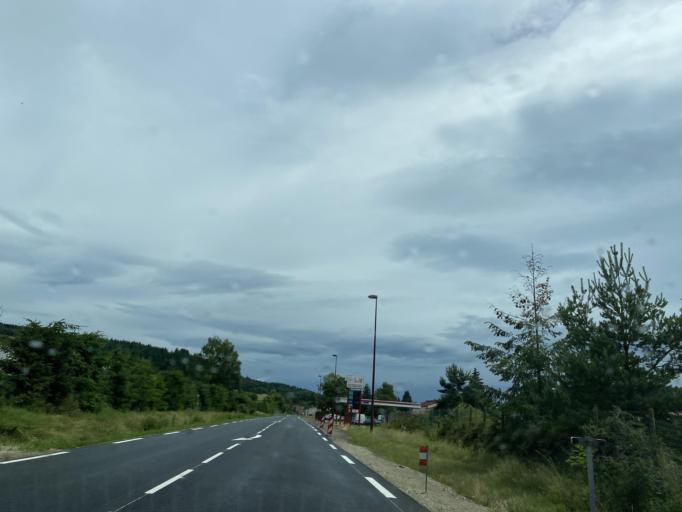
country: FR
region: Rhone-Alpes
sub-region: Departement de la Loire
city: Noiretable
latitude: 45.8104
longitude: 3.7931
